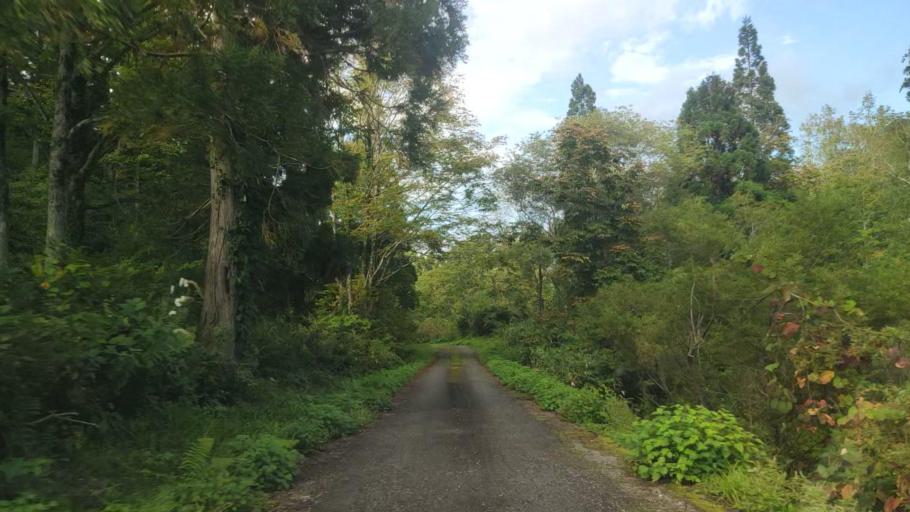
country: JP
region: Toyama
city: Yatsuomachi-higashikumisaka
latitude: 36.3627
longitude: 137.0714
